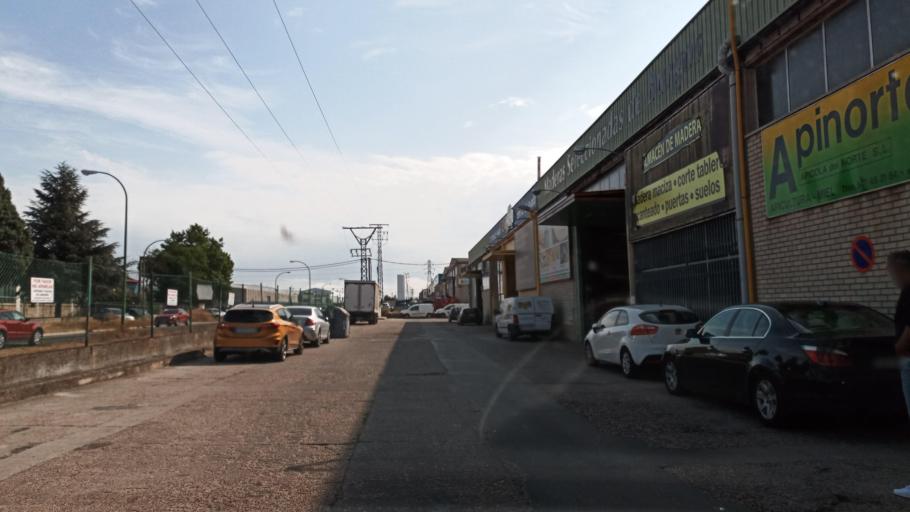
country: ES
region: Castille and Leon
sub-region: Provincia de Burgos
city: Burgos
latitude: 42.3594
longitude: -3.6561
